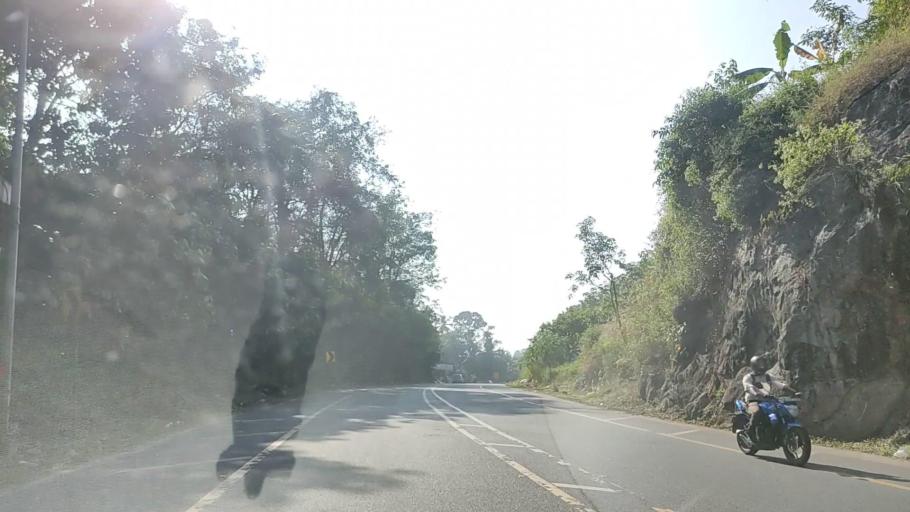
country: IN
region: Kerala
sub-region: Kollam
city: Punalur
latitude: 8.8910
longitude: 76.8666
